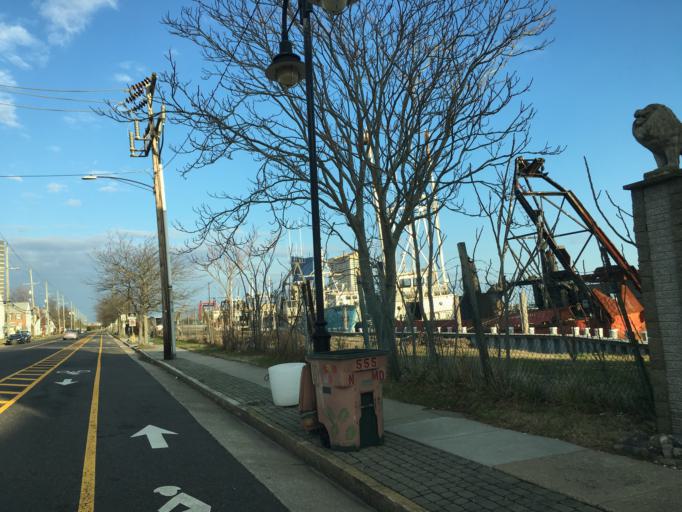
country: US
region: New Jersey
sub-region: Atlantic County
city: Atlantic City
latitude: 39.3724
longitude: -74.4270
